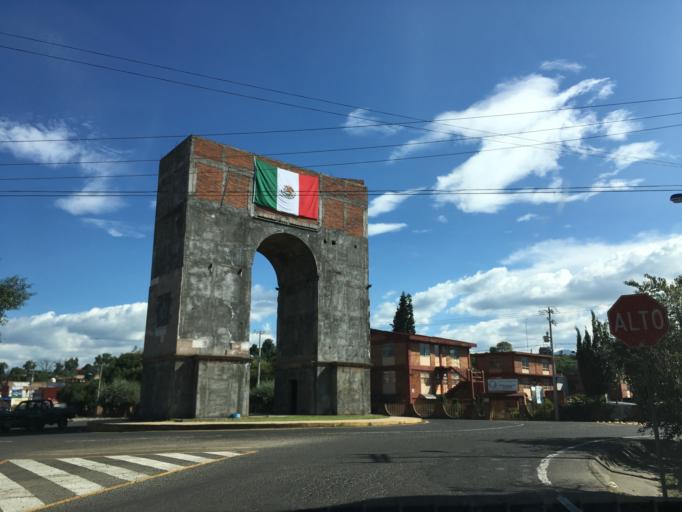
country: MX
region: Michoacan
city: Zacapu
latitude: 19.8078
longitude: -101.7827
